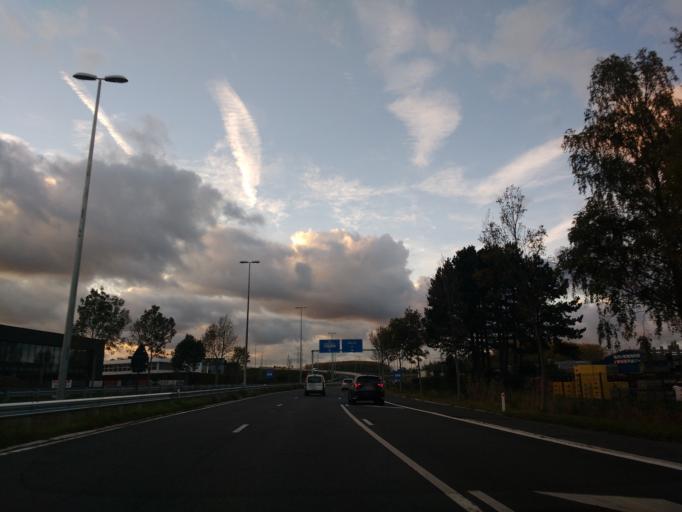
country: BE
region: Flanders
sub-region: Provincie West-Vlaanderen
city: Brugge
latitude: 51.2120
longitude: 3.1944
